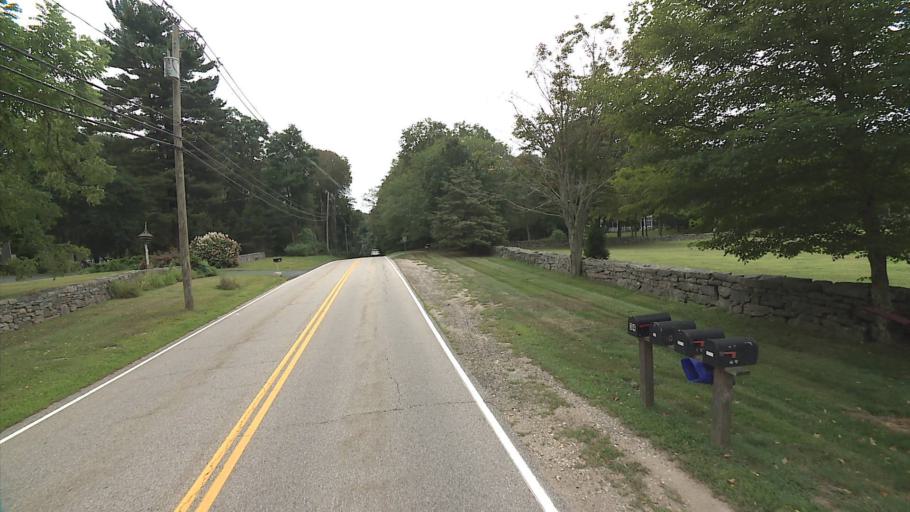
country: US
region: Connecticut
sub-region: Middlesex County
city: Essex Village
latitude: 41.3568
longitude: -72.3415
